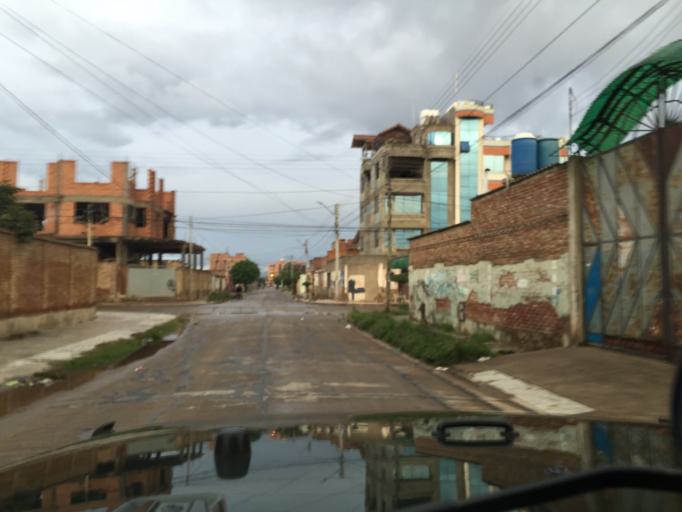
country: BO
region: Cochabamba
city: Cochabamba
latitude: -17.4193
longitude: -66.1634
